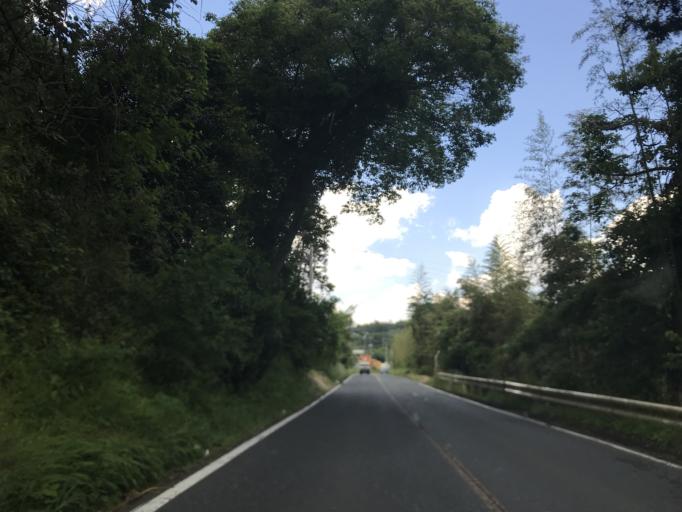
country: JP
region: Miyagi
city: Wakuya
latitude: 38.5597
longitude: 141.1358
